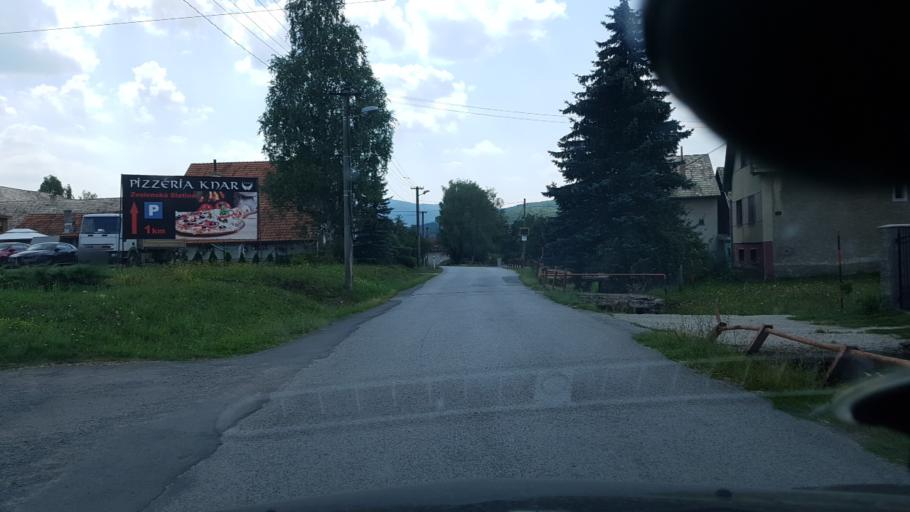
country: SK
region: Banskobystricky
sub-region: Okres Banska Bystrica
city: Zvolen
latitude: 48.5688
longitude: 19.2548
